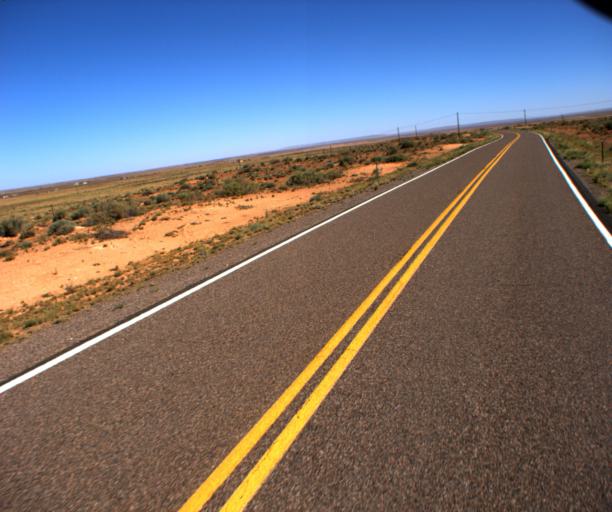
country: US
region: Arizona
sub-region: Coconino County
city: LeChee
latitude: 35.1203
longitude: -110.8737
